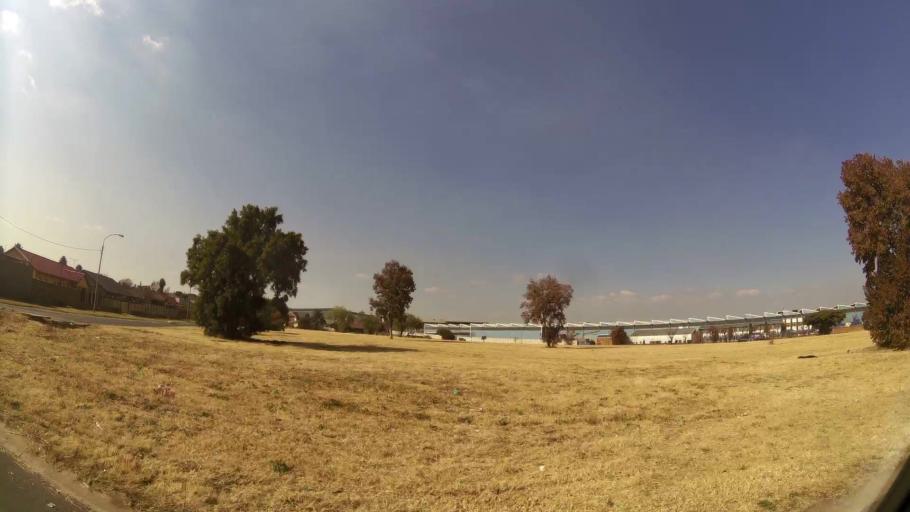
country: ZA
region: Gauteng
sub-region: Ekurhuleni Metropolitan Municipality
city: Boksburg
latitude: -26.1910
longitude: 28.2136
